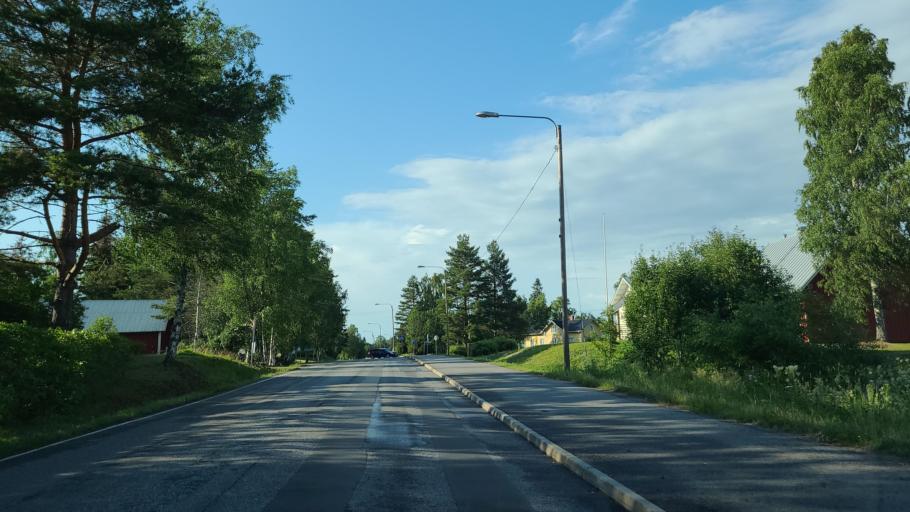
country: FI
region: Ostrobothnia
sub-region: Vaasa
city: Replot
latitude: 63.2269
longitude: 21.4111
